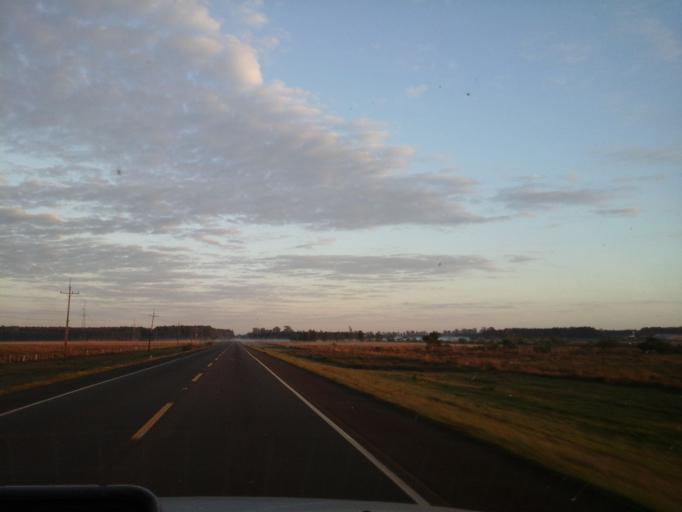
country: PY
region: Itapua
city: General Delgado
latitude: -27.0670
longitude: -56.6150
